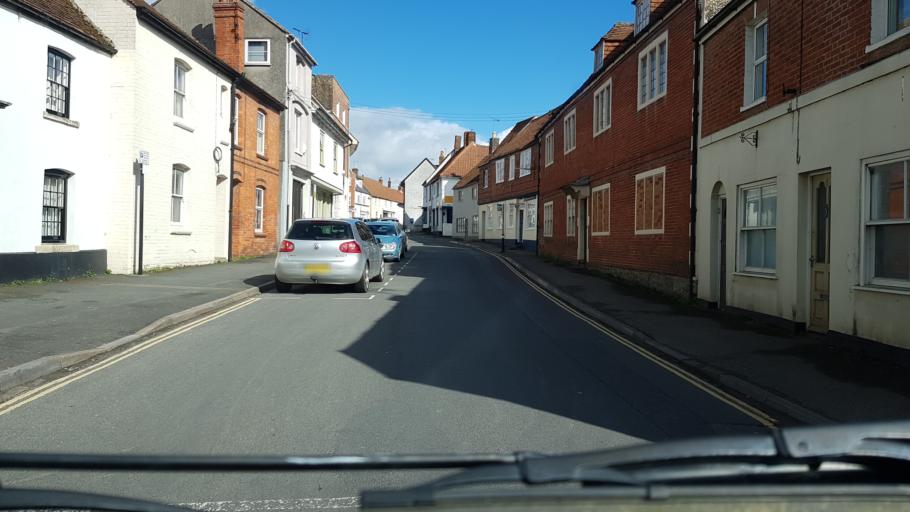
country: GB
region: England
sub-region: Wiltshire
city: Market Lavington
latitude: 51.2864
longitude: -1.9793
